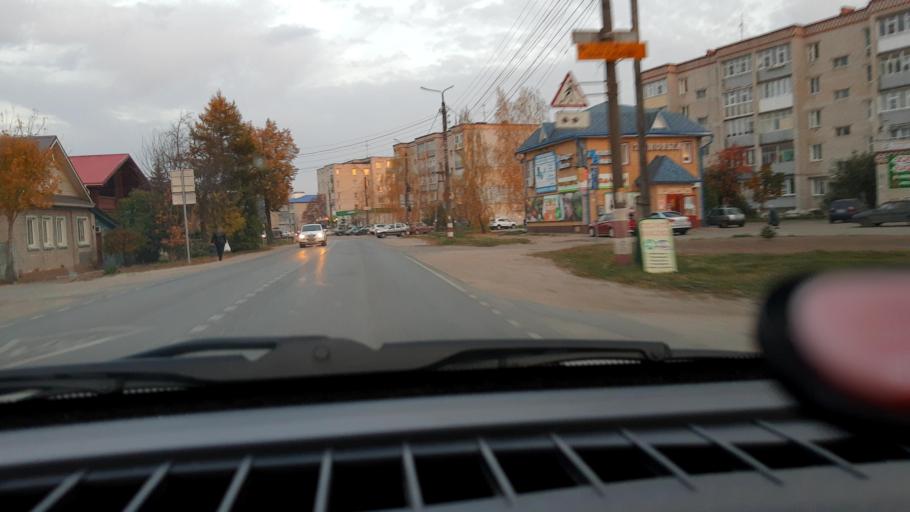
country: RU
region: Nizjnij Novgorod
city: Gorodets
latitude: 56.6402
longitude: 43.4817
